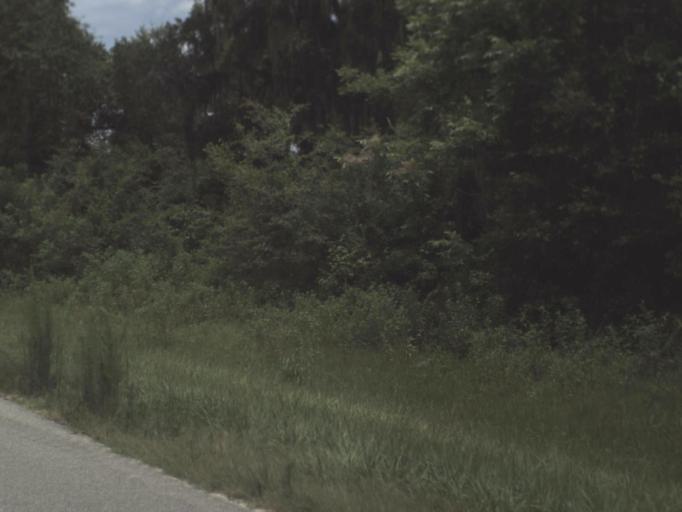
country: US
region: Florida
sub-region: Madison County
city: Madison
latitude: 30.5493
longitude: -83.4258
